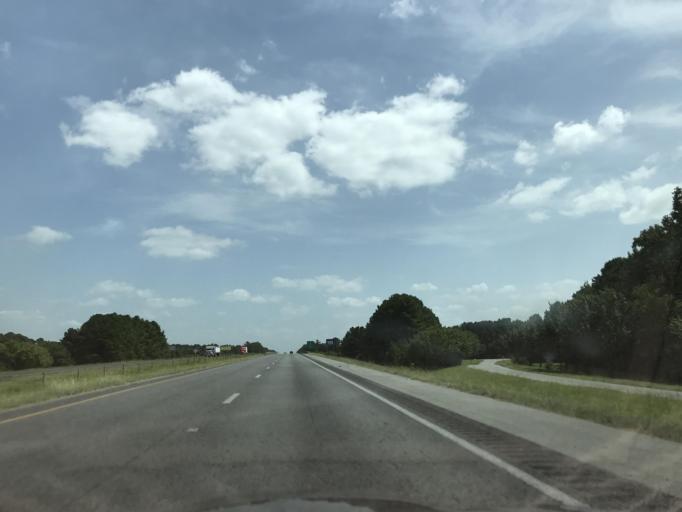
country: US
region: North Carolina
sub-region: Duplin County
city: Wallace
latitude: 34.7716
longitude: -77.9673
